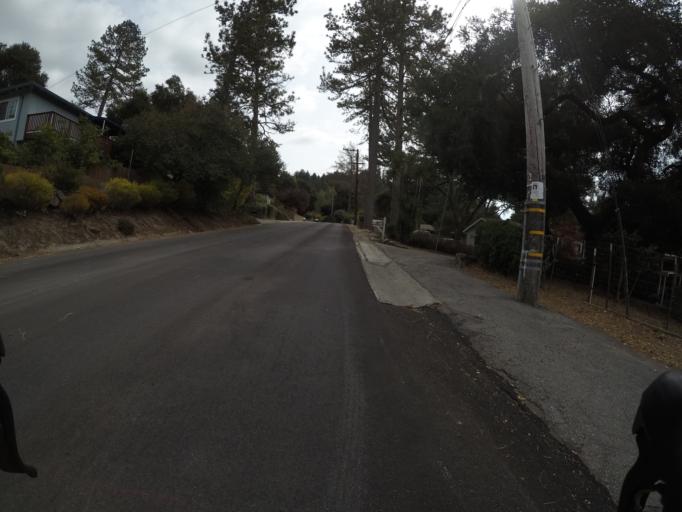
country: US
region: California
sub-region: Santa Cruz County
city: Ben Lomond
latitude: 37.0773
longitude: -122.0791
